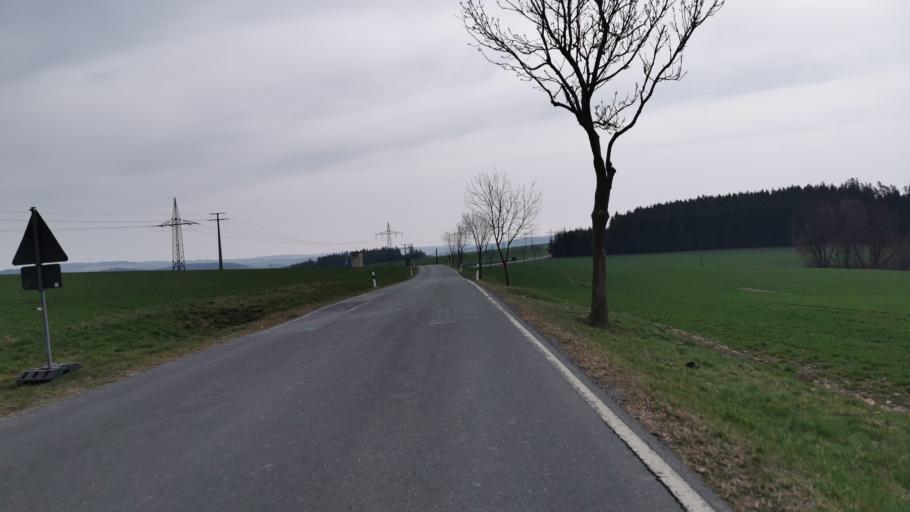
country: DE
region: Thuringia
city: Leutenberg
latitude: 50.5326
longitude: 11.4345
